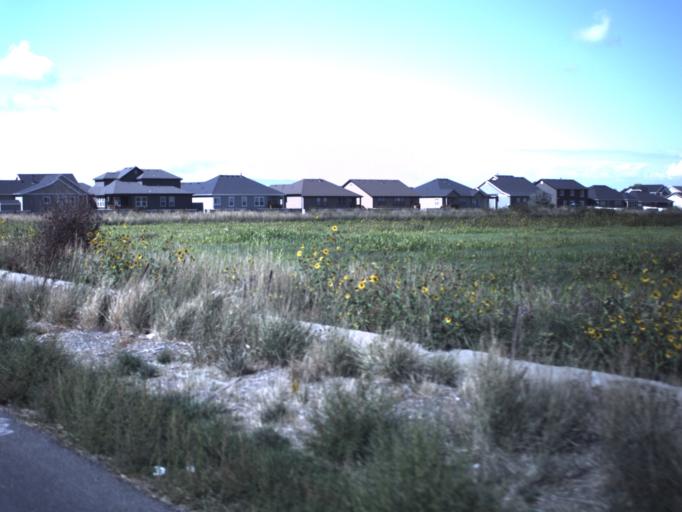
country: US
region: Utah
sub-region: Utah County
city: Spanish Fork
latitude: 40.1154
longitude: -111.6180
